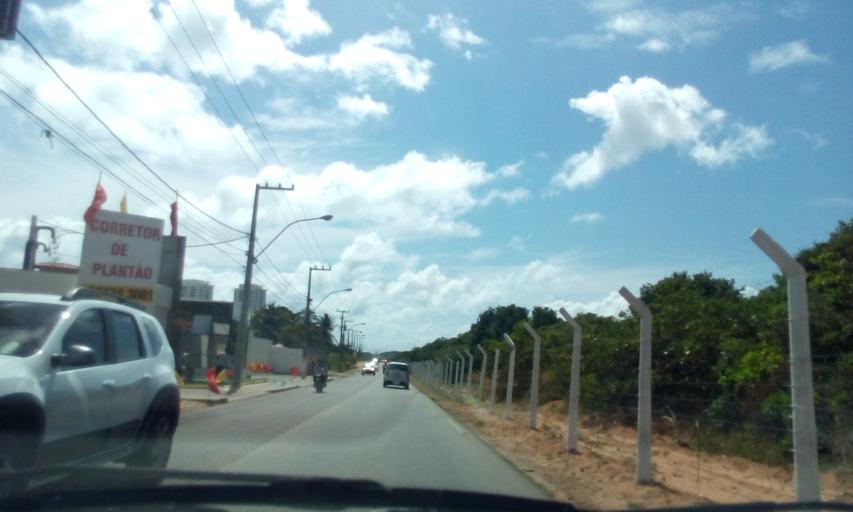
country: BR
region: Rio Grande do Norte
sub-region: Parnamirim
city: Parnamirim
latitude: -5.8905
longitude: -35.1841
